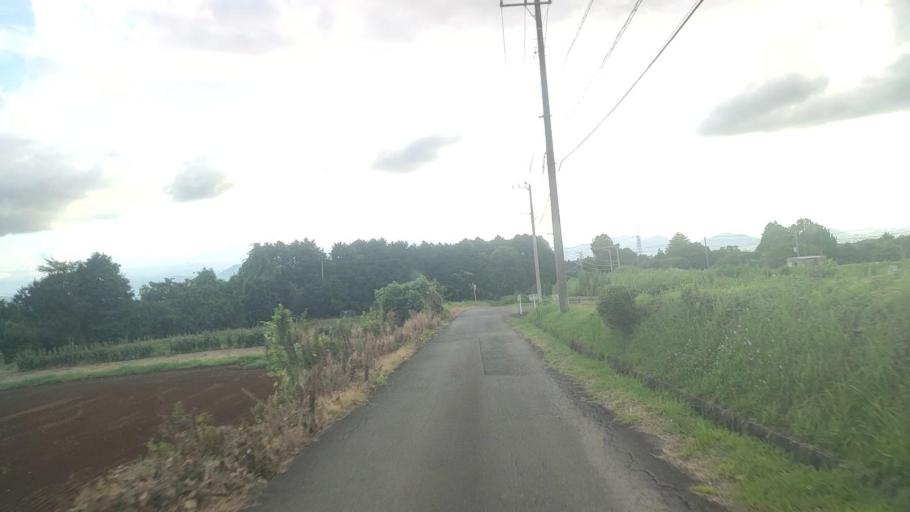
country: JP
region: Kanagawa
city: Hakone
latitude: 35.1260
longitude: 138.9900
